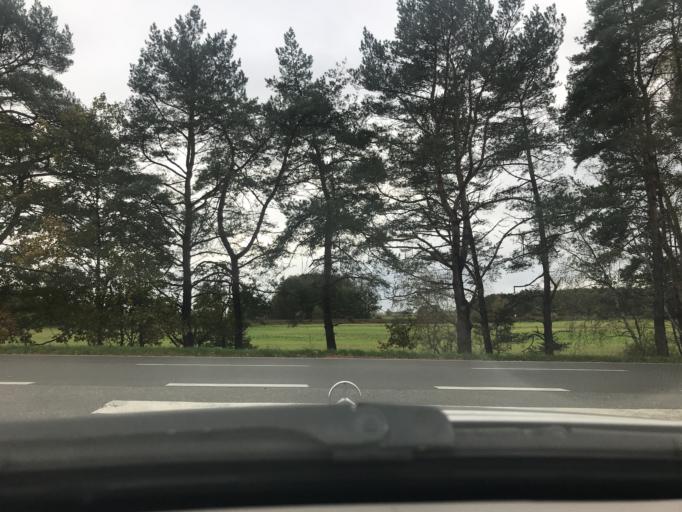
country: DE
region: Mecklenburg-Vorpommern
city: Ostseebad Zinnowitz
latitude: 54.0690
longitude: 13.9386
